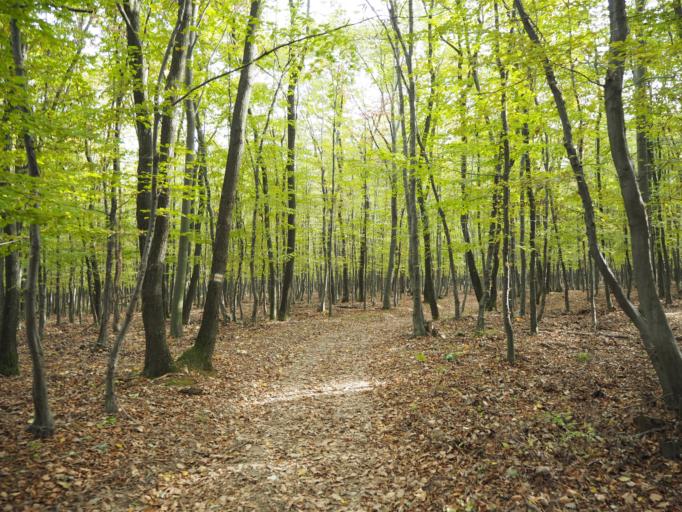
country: HU
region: Baranya
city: Pecsvarad
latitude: 46.1765
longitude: 18.4006
